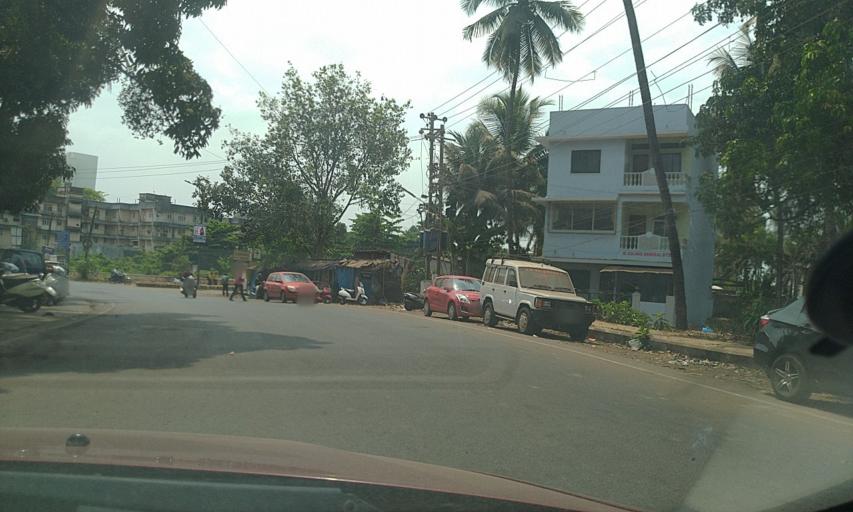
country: IN
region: Goa
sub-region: North Goa
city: Mapuca
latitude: 15.5918
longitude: 73.8072
